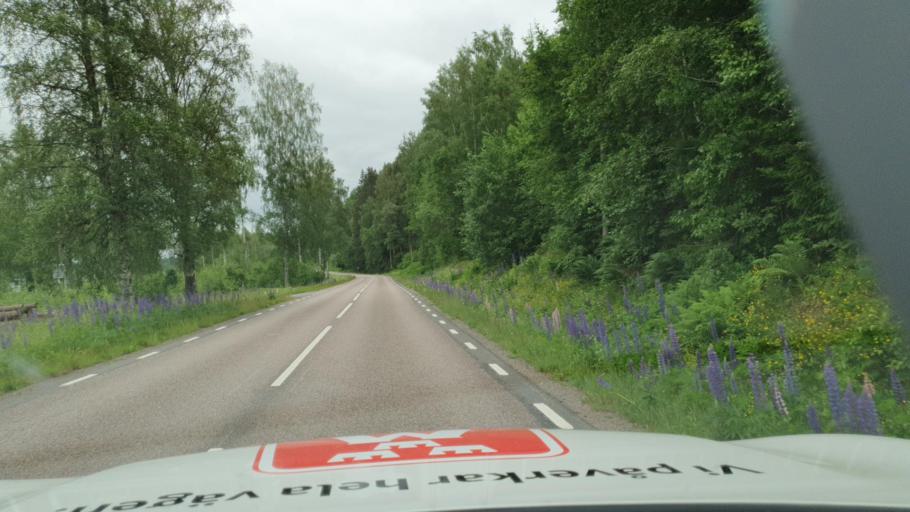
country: SE
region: Vaermland
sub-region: Sunne Kommun
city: Sunne
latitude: 59.8207
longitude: 13.0027
